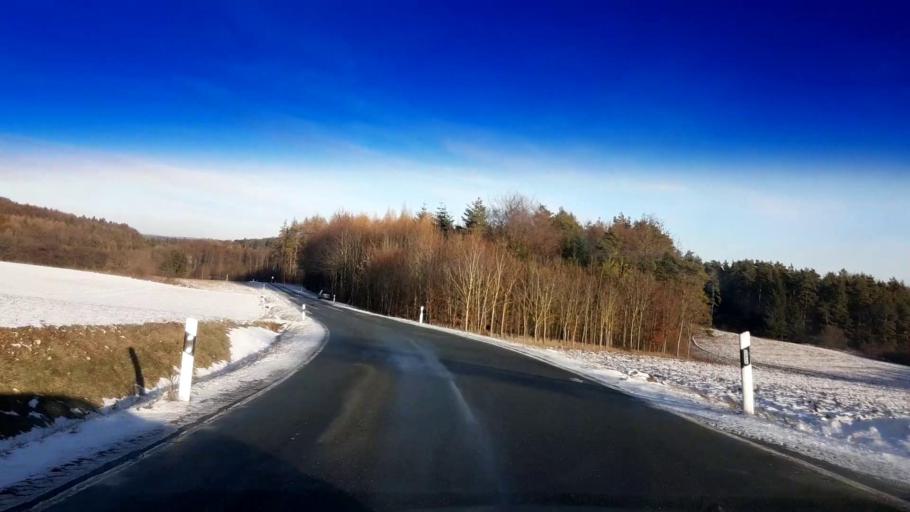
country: DE
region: Bavaria
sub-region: Upper Franconia
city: Heiligenstadt
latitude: 49.8488
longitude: 11.1400
